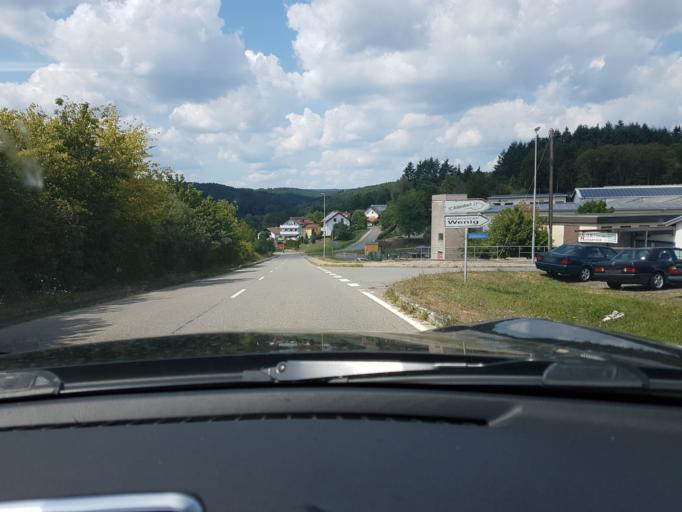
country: DE
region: Baden-Wuerttemberg
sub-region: Karlsruhe Region
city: Limbach
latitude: 49.4238
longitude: 9.2393
